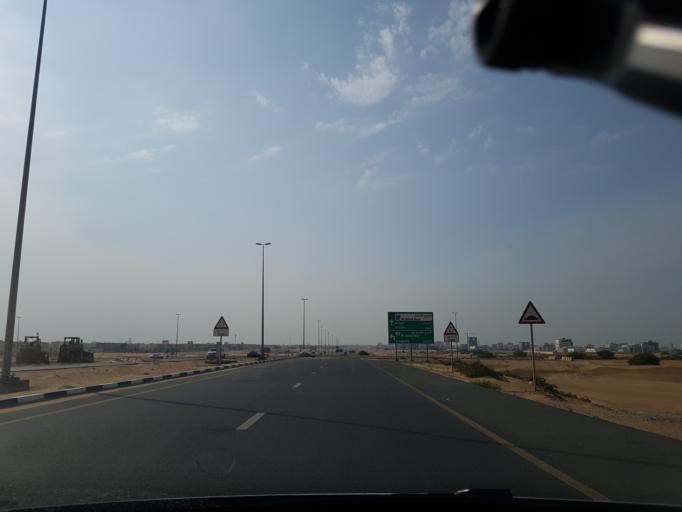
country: AE
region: Ajman
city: Ajman
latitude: 25.4134
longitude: 55.5583
